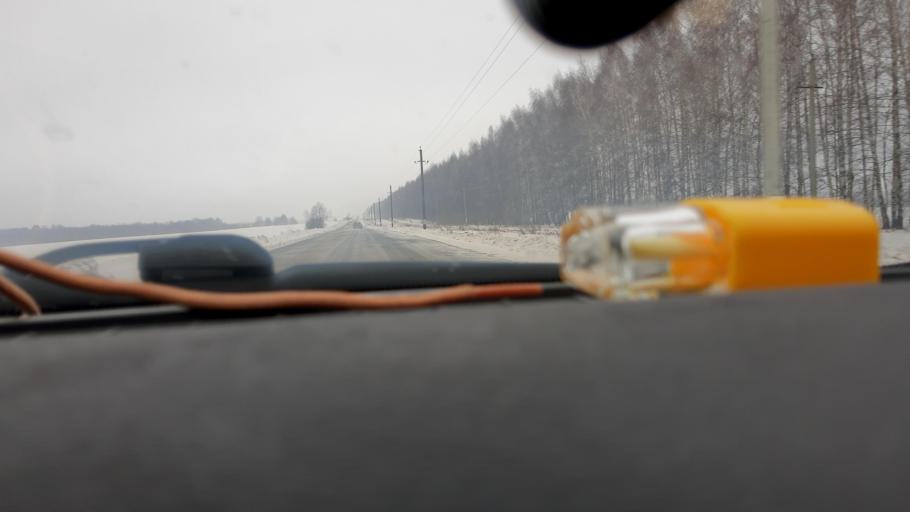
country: RU
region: Bashkortostan
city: Ulukulevo
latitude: 54.5801
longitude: 56.4261
